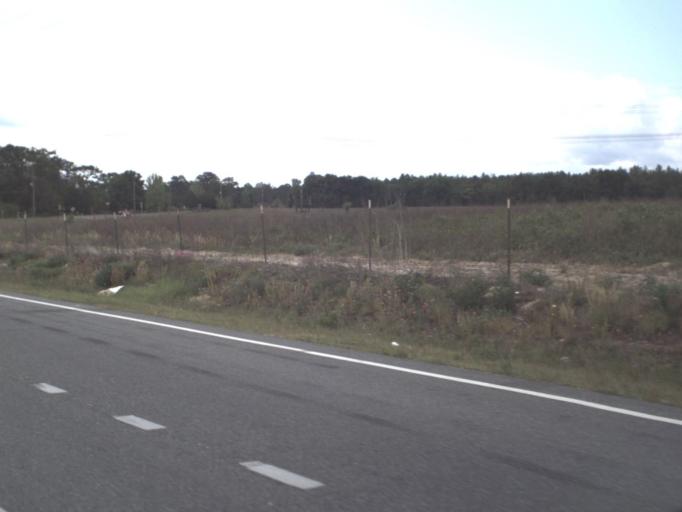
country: US
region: Florida
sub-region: Marion County
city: Ocala
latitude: 29.2423
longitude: -82.0549
